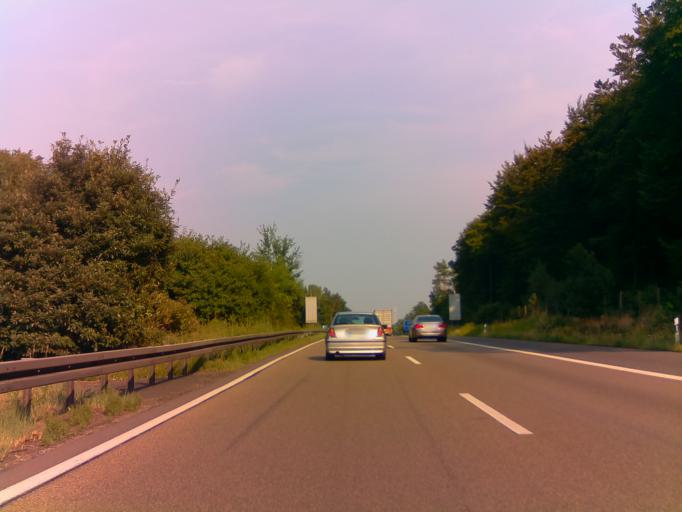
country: DE
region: Hesse
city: Kirtorf
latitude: 50.7165
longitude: 9.0899
